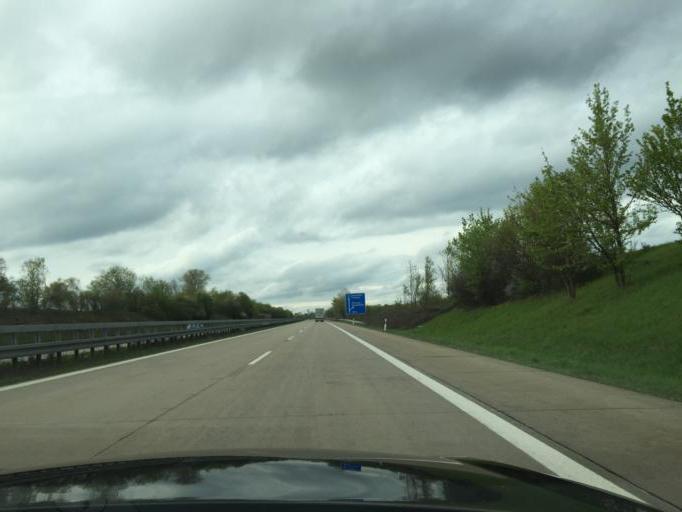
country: DE
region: Baden-Wuerttemberg
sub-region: Regierungsbezirk Stuttgart
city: Ellwangen
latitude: 48.9475
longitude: 10.1901
